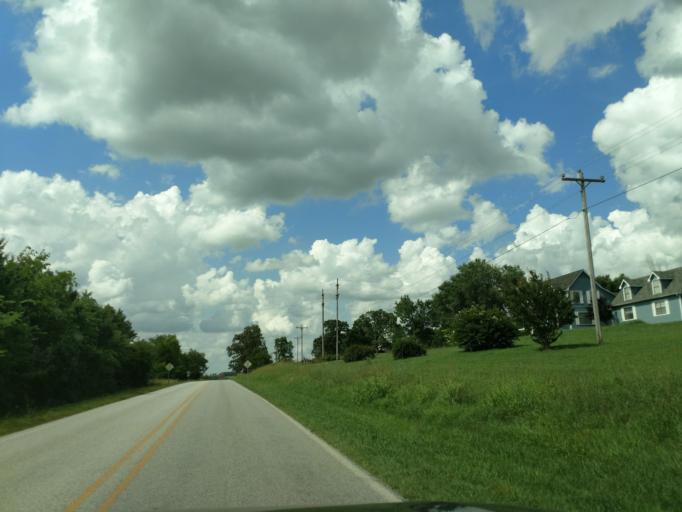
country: US
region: Arkansas
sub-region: Carroll County
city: Berryville
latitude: 36.3937
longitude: -93.5661
